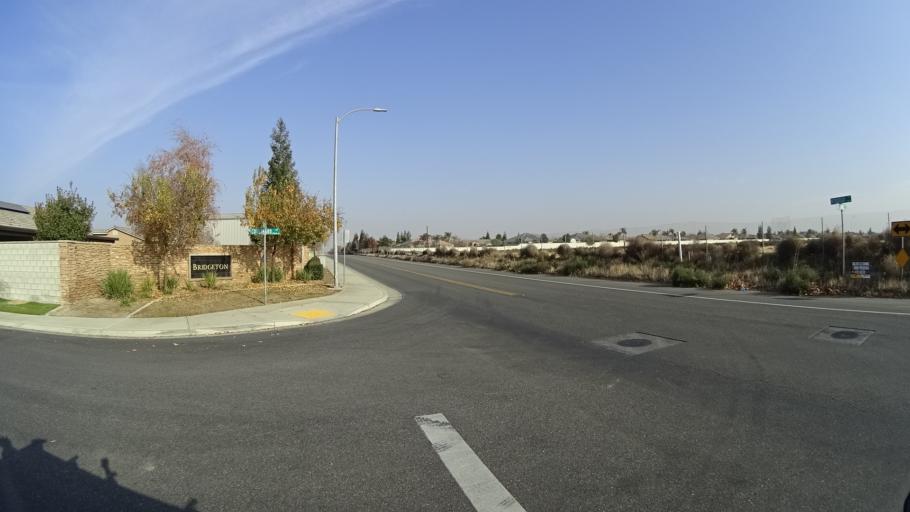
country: US
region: California
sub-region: Kern County
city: Greenacres
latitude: 35.4310
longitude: -119.1191
